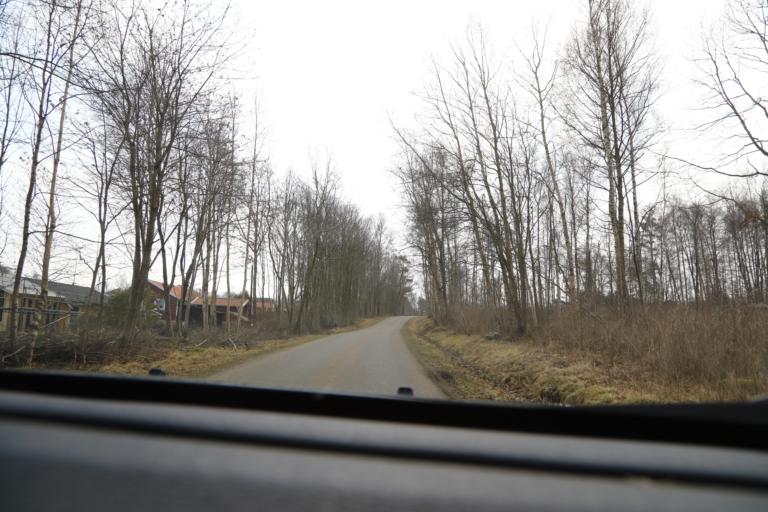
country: SE
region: Halland
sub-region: Kungsbacka Kommun
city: Frillesas
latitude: 57.2776
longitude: 12.1408
